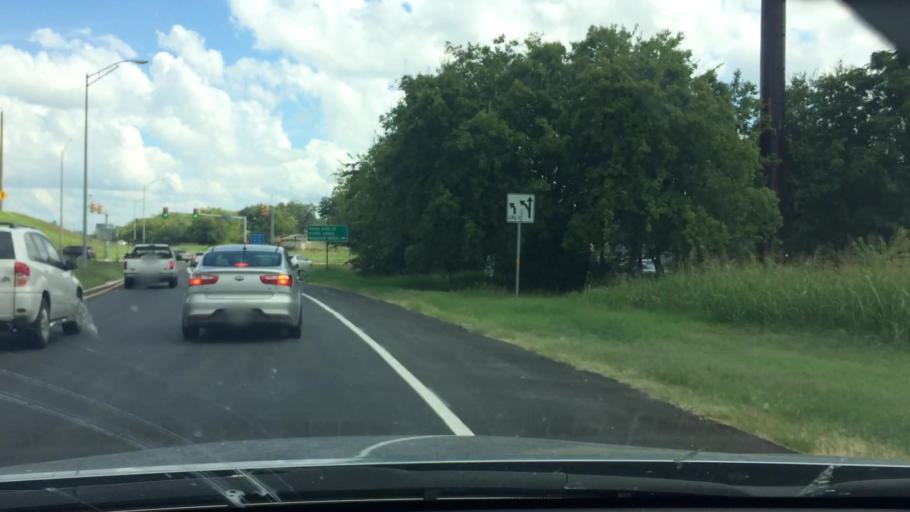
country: US
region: Texas
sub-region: Bexar County
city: San Antonio
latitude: 29.3625
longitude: -98.4438
